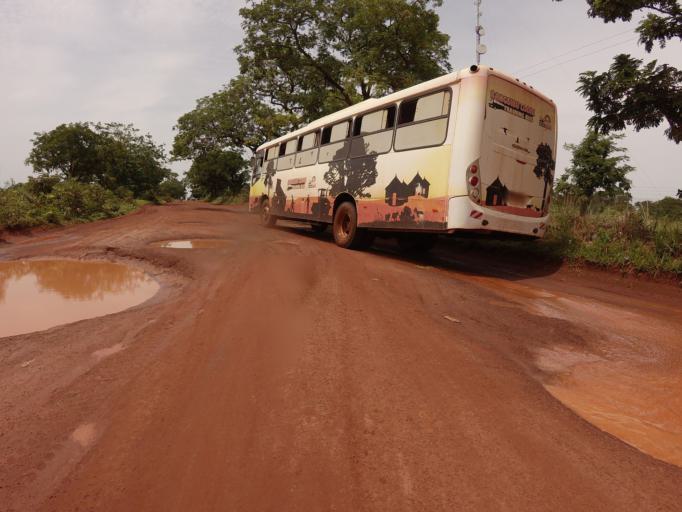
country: GH
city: Kpandae
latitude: 8.8720
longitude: 0.0445
